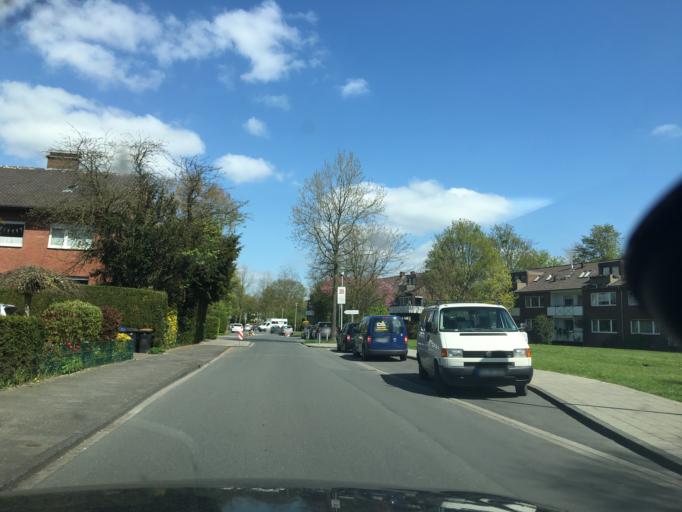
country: DE
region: North Rhine-Westphalia
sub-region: Regierungsbezirk Munster
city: Muenster
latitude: 51.9742
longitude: 7.6460
